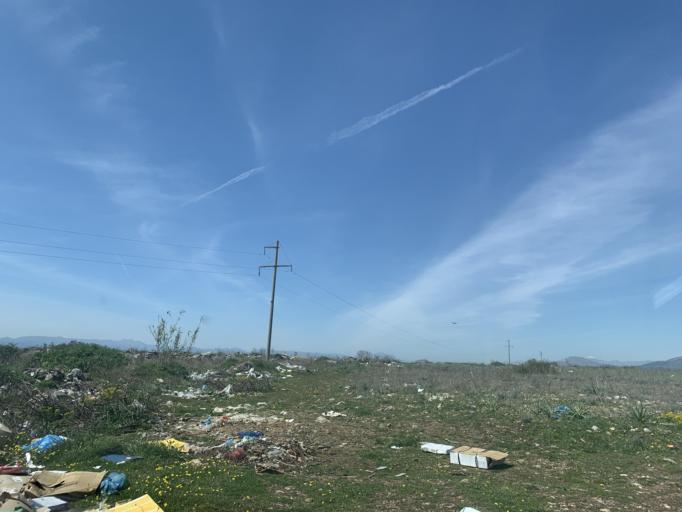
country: AL
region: Shkoder
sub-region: Rrethi i Malesia e Madhe
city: Koplik
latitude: 42.2295
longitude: 19.4358
